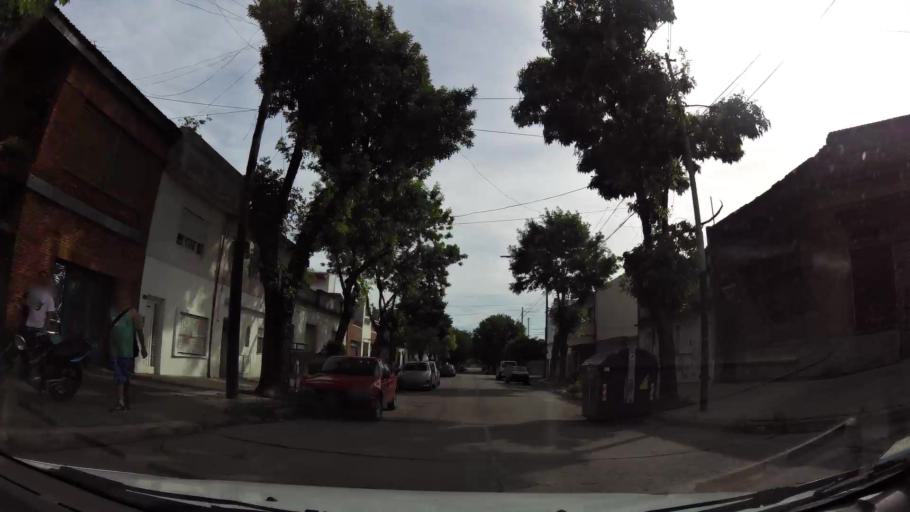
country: AR
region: Buenos Aires F.D.
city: Villa Lugano
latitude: -34.6524
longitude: -58.4799
